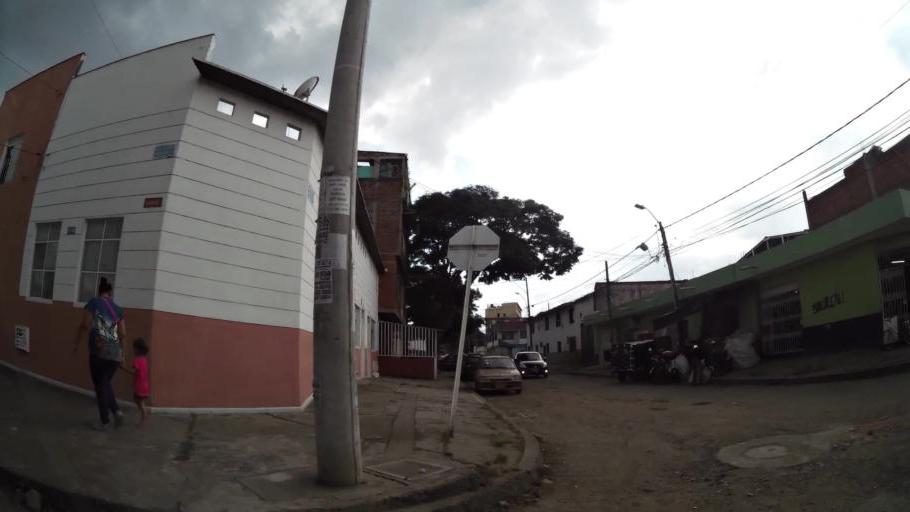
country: CO
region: Valle del Cauca
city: Cali
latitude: 3.4742
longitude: -76.5077
